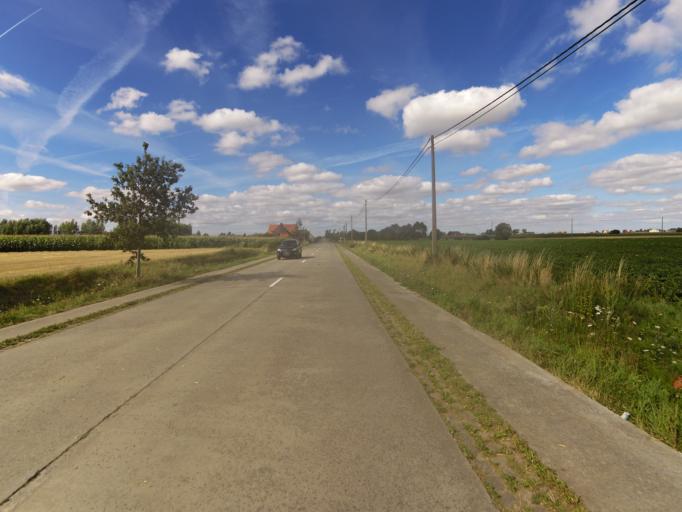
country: FR
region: Nord-Pas-de-Calais
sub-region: Departement du Nord
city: Steenvoorde
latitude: 50.8694
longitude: 2.6213
